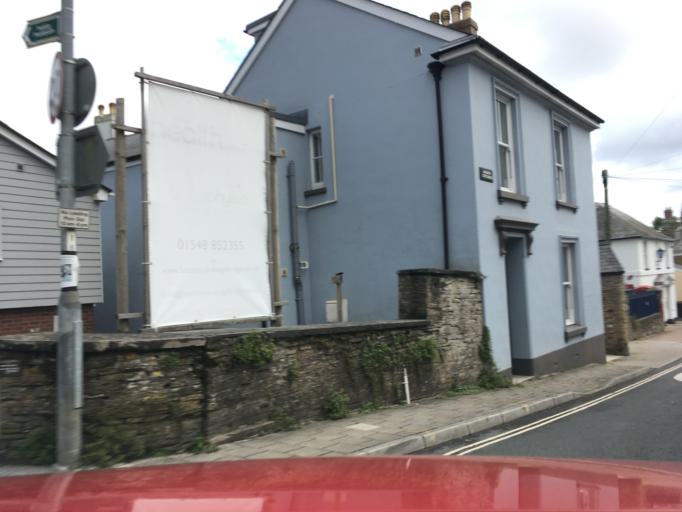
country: GB
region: England
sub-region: Devon
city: Kingsbridge
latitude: 50.2889
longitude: -3.7776
